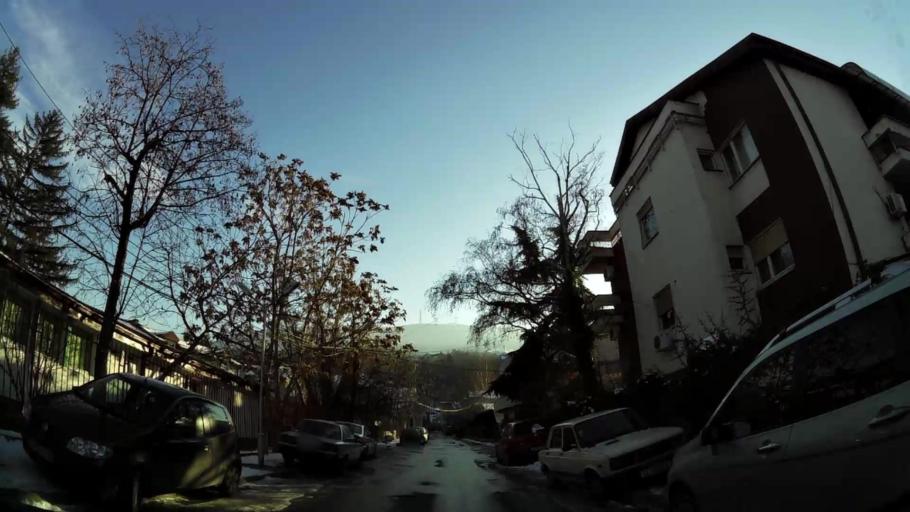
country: MK
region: Karpos
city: Skopje
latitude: 41.9929
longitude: 21.4027
